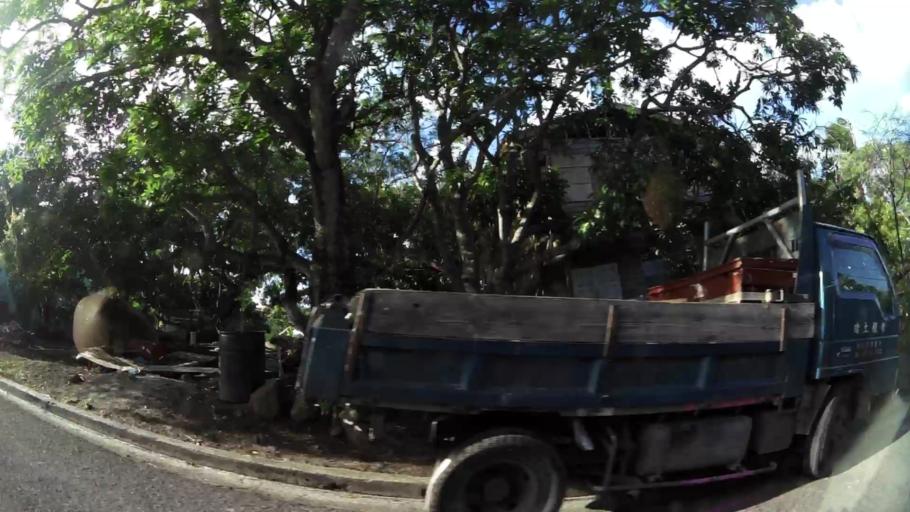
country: AG
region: Saint Peter
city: All Saints
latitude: 17.0450
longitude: -61.8162
